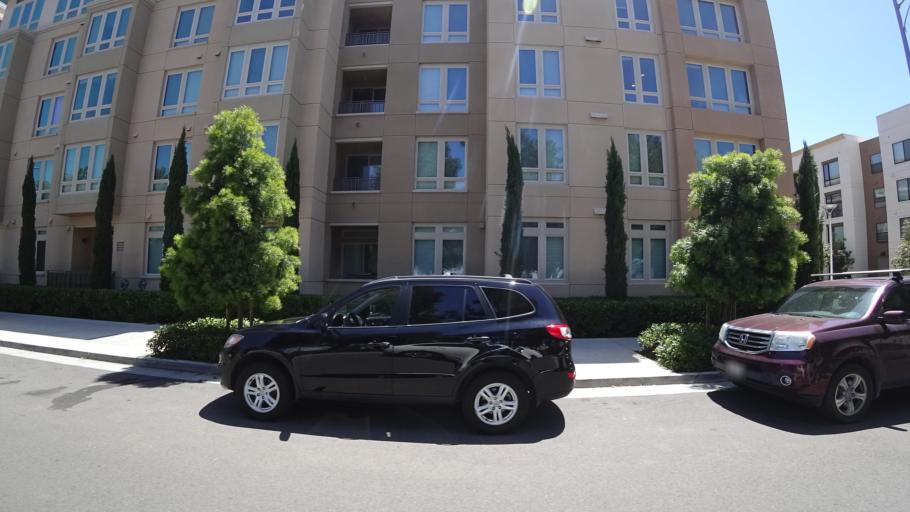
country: US
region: California
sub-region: Santa Clara County
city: Milpitas
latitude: 37.4042
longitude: -121.9432
